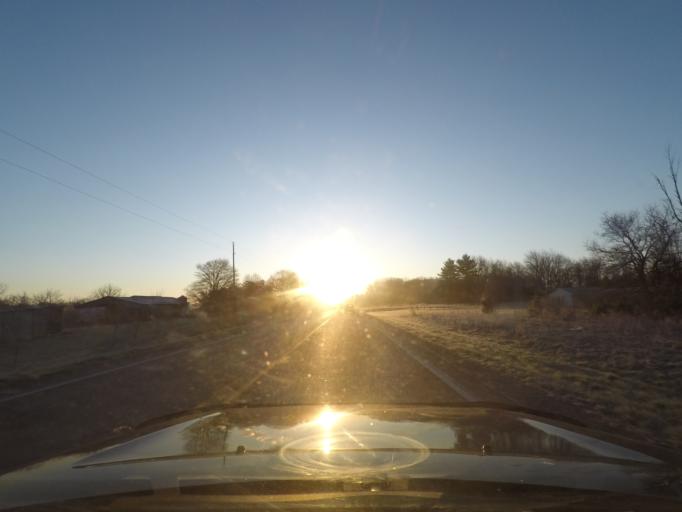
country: US
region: Indiana
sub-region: Marshall County
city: Plymouth
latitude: 41.4491
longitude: -86.3221
